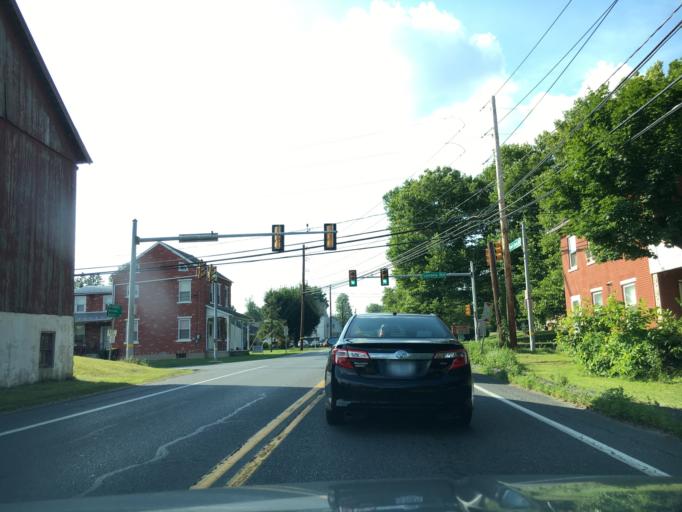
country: US
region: Pennsylvania
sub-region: Lehigh County
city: Egypt
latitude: 40.6644
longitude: -75.5639
